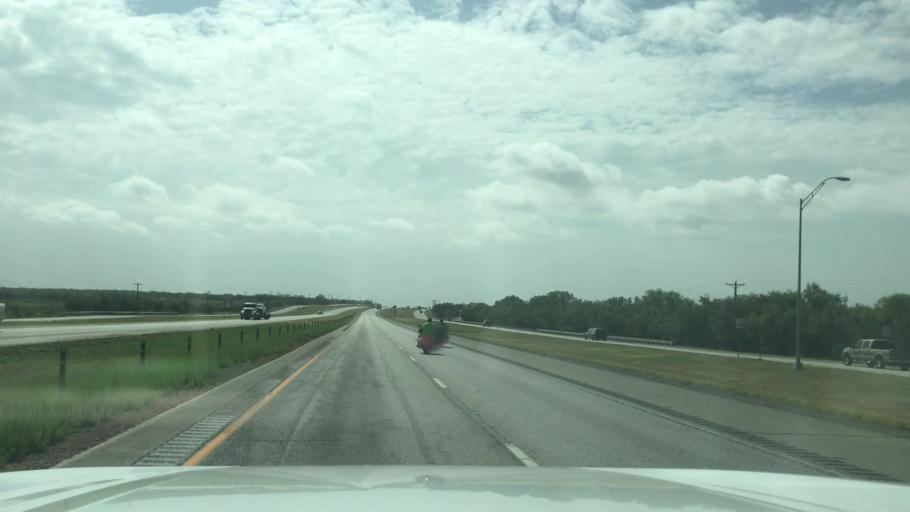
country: US
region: Texas
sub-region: Taylor County
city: Abilene
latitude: 32.4731
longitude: -99.6933
